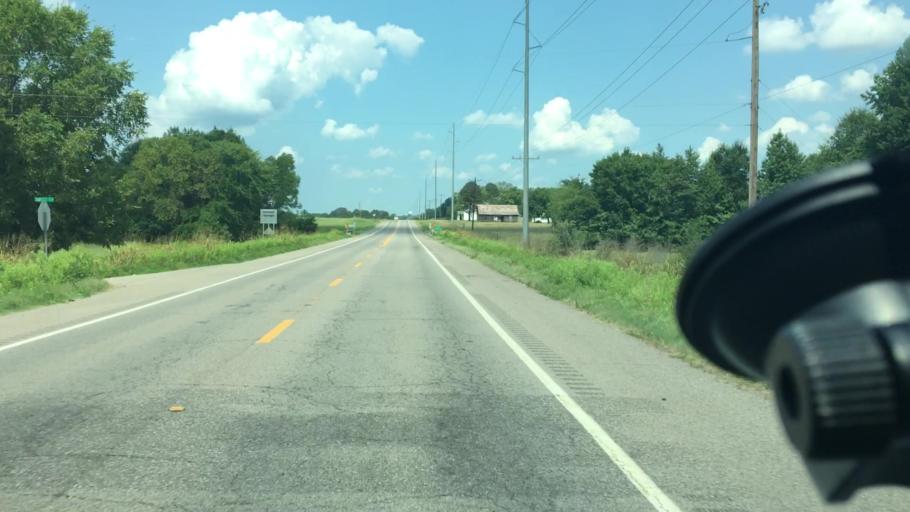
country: US
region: Arkansas
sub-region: Logan County
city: Paris
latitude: 35.2946
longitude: -93.6554
